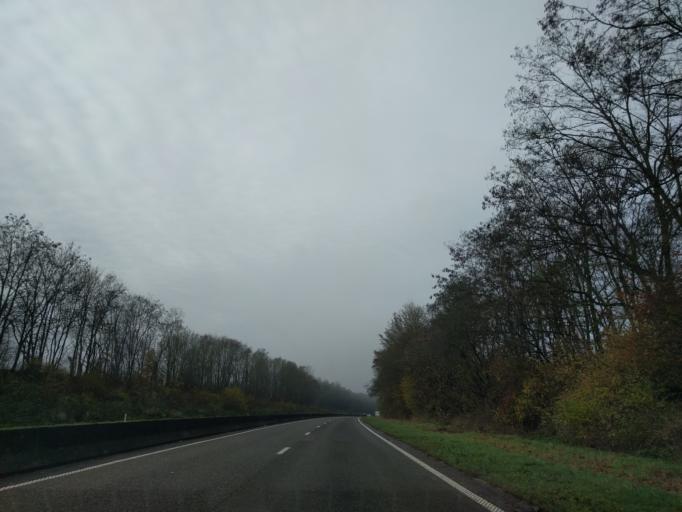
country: BE
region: Wallonia
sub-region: Province de Namur
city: Onhaye
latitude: 50.2420
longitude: 4.8666
